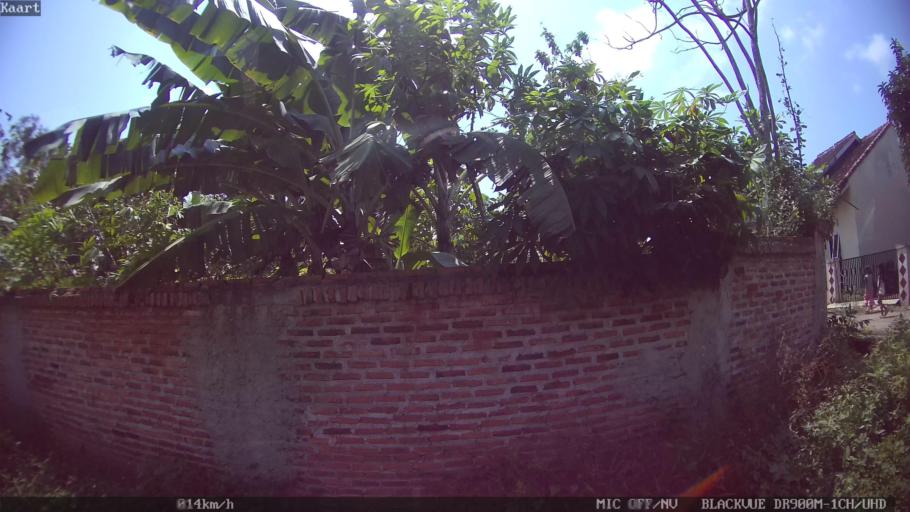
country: ID
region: Lampung
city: Kedaton
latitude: -5.3516
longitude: 105.2790
